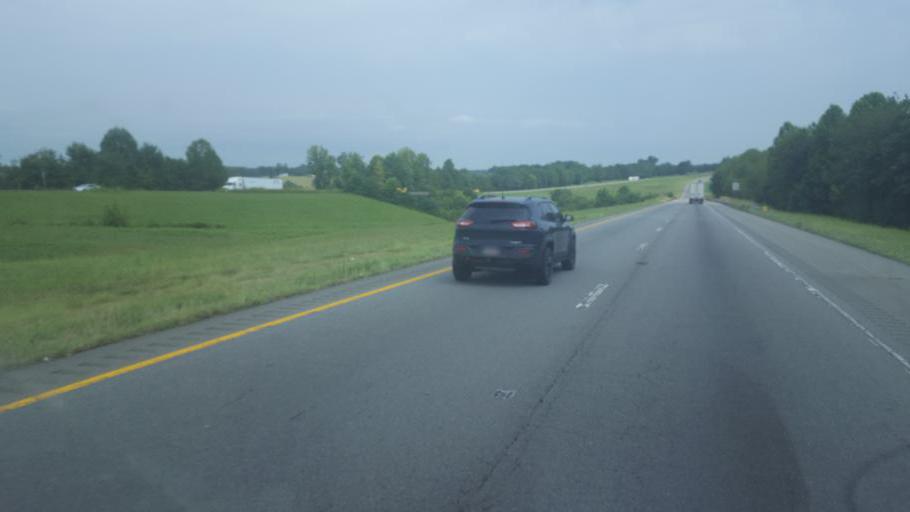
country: US
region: North Carolina
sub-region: Iredell County
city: Statesville
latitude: 35.9260
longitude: -80.8550
